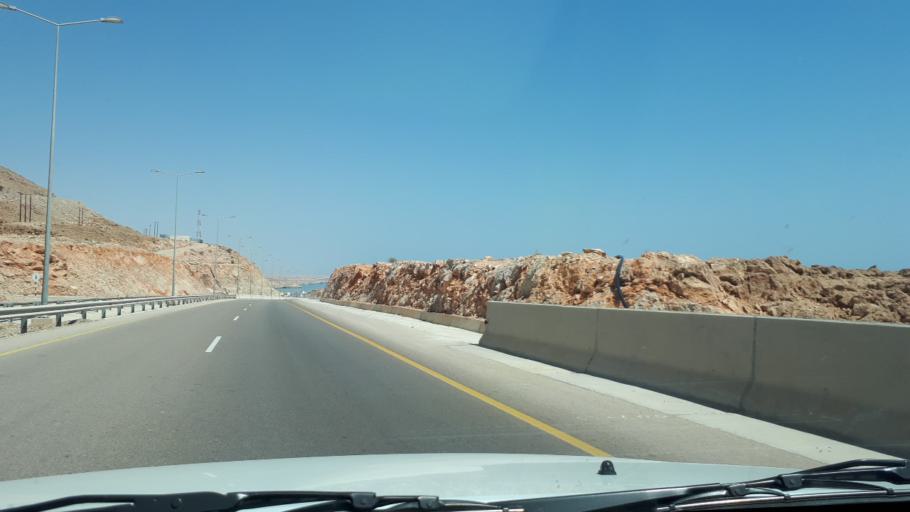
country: OM
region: Ash Sharqiyah
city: Sur
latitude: 22.8322
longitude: 59.2496
